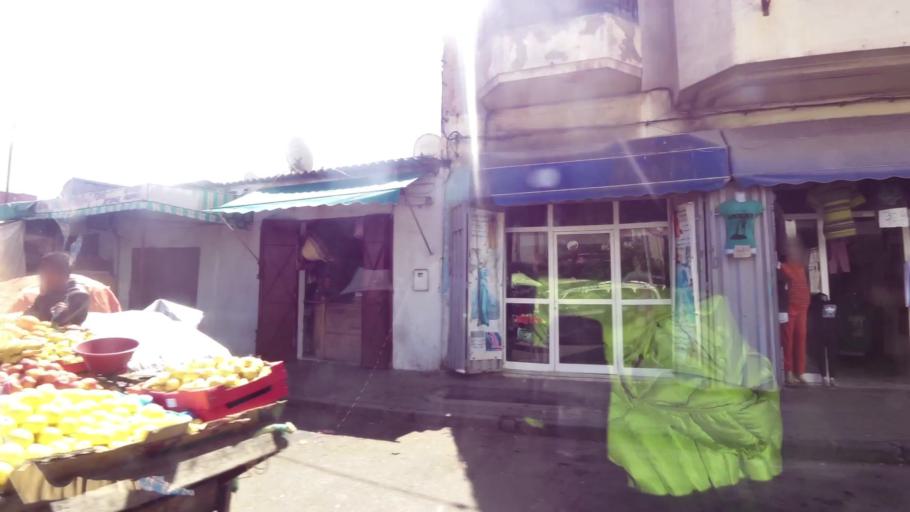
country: MA
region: Grand Casablanca
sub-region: Casablanca
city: Casablanca
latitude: 33.5980
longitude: -7.6247
